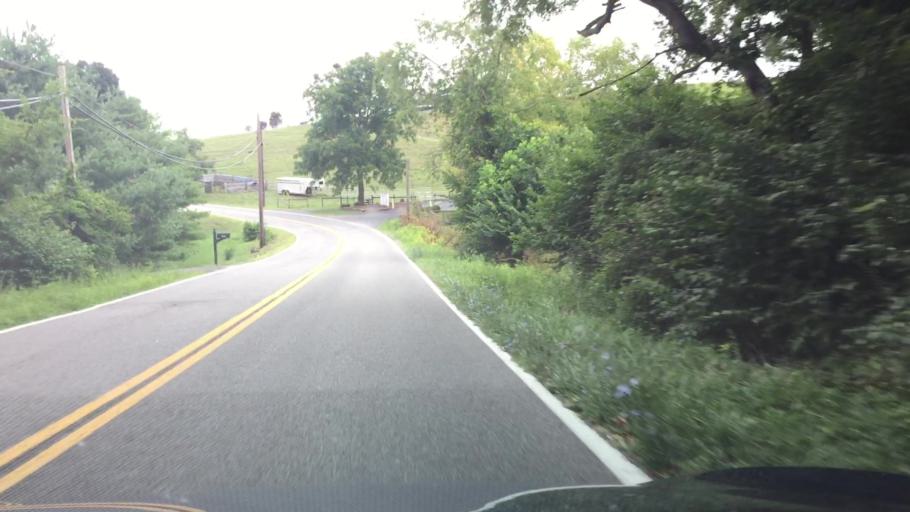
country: US
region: Virginia
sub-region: Pulaski County
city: Pulaski
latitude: 37.0105
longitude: -80.7436
